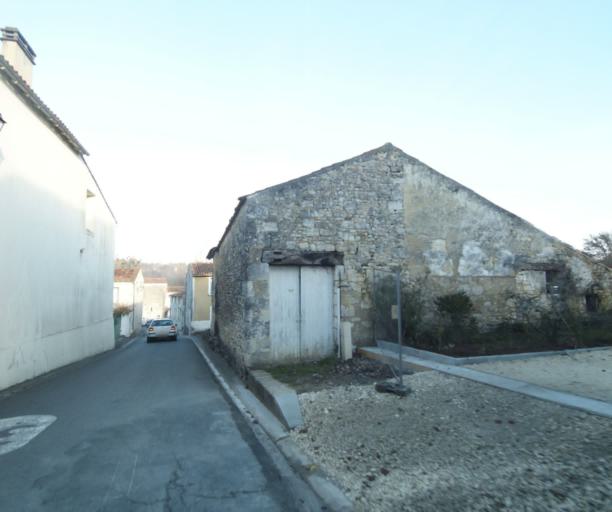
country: FR
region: Poitou-Charentes
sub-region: Departement de la Charente-Maritime
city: Fontcouverte
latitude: 45.7709
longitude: -0.5917
